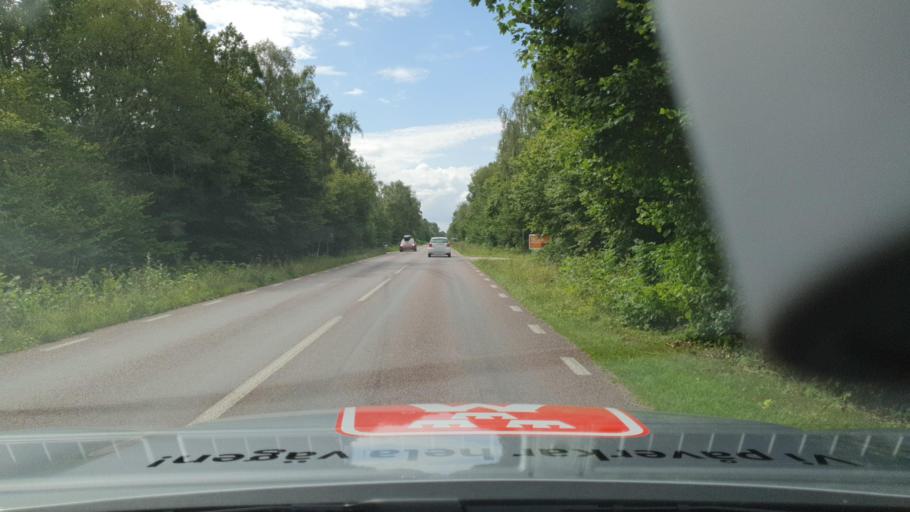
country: SE
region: Gotland
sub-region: Gotland
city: Hemse
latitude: 57.0548
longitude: 18.2938
